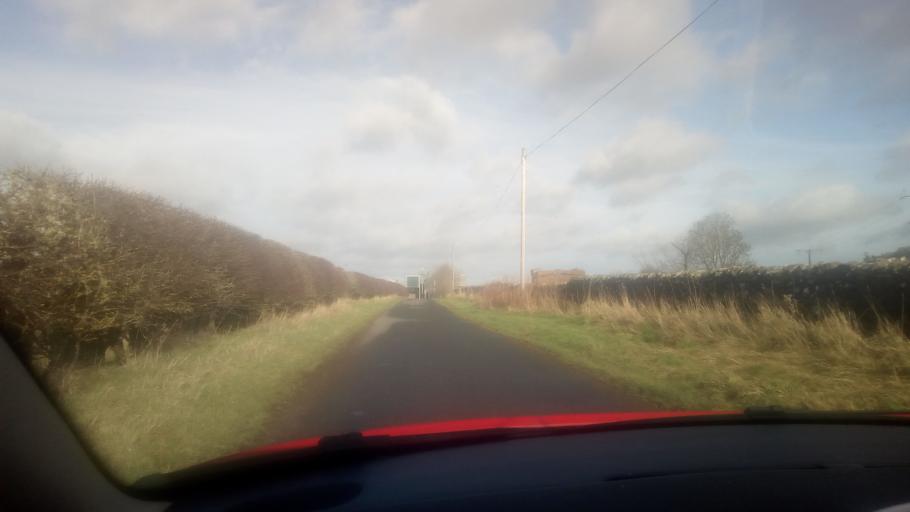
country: GB
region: Scotland
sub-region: The Scottish Borders
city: Kelso
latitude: 55.5020
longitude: -2.4234
